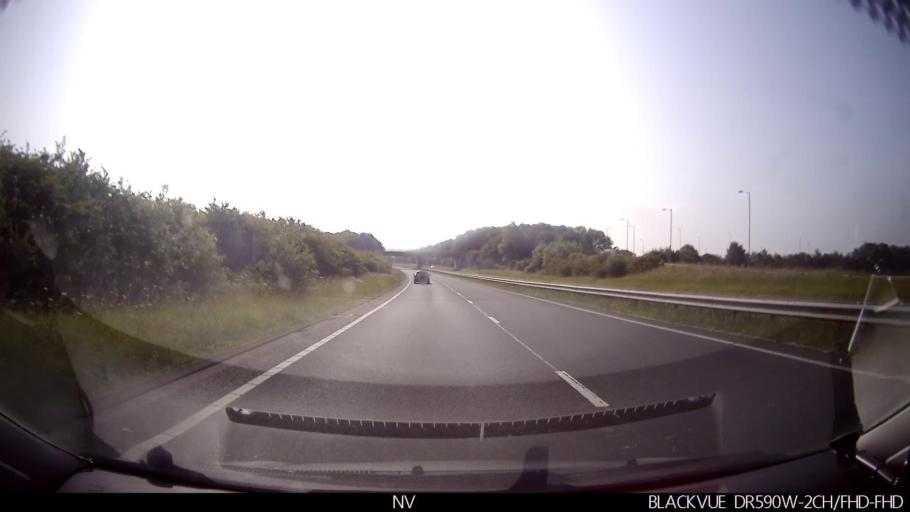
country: GB
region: England
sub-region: North Yorkshire
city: Malton
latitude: 54.1430
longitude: -0.7513
